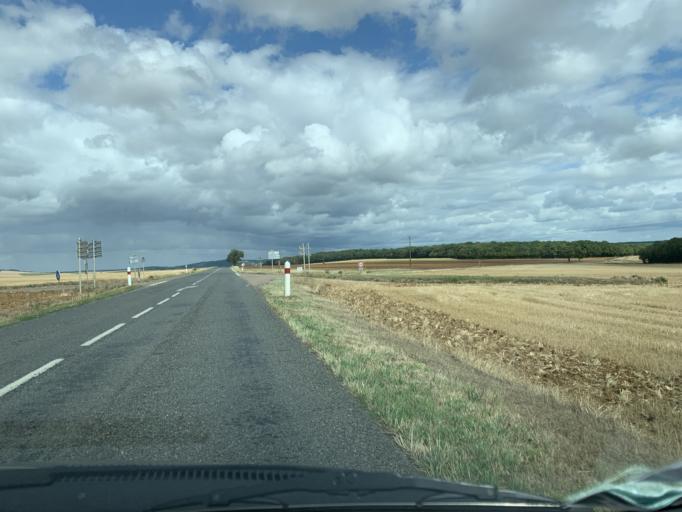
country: FR
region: Bourgogne
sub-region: Departement de la Nievre
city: Clamecy
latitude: 47.4203
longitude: 3.4658
